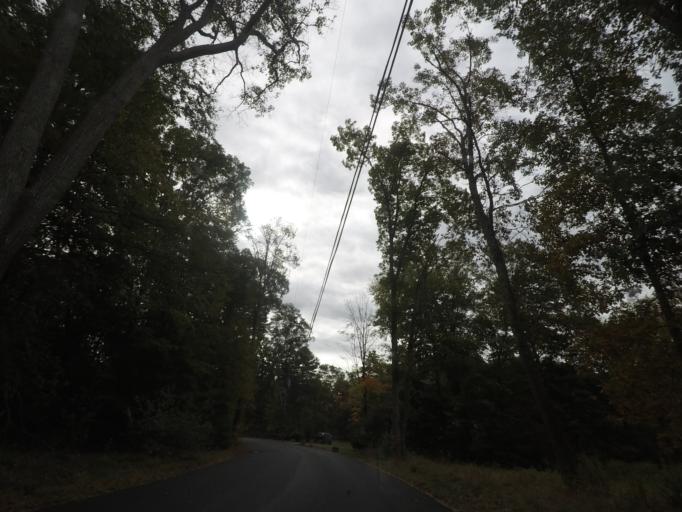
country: US
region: Connecticut
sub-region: Windham County
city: Thompson
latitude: 41.9720
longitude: -71.8380
